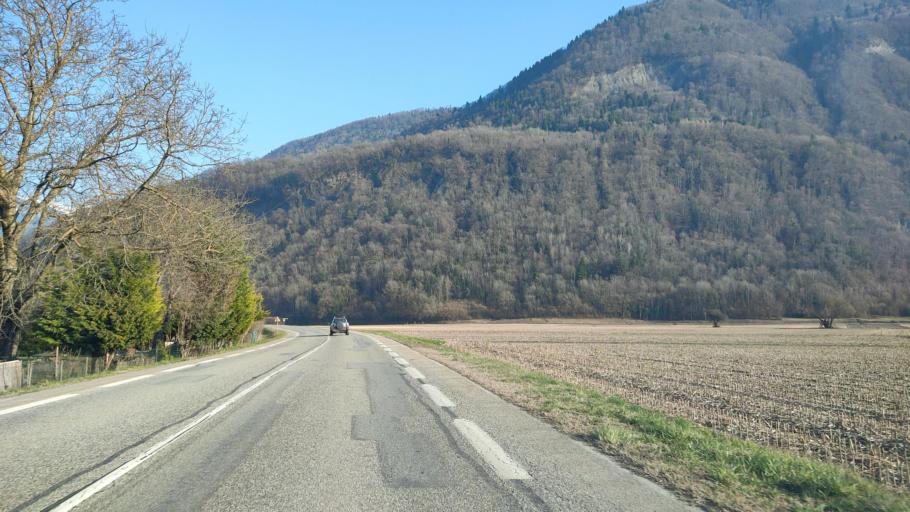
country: FR
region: Rhone-Alpes
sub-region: Departement de la Savoie
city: Aiton
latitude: 45.5500
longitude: 6.2350
